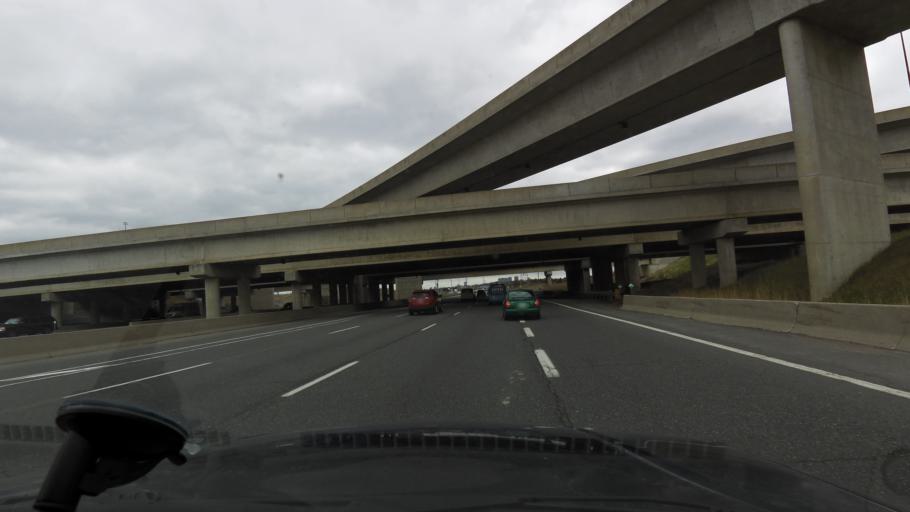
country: CA
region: Ontario
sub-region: York
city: Richmond Hill
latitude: 43.8397
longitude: -79.3689
